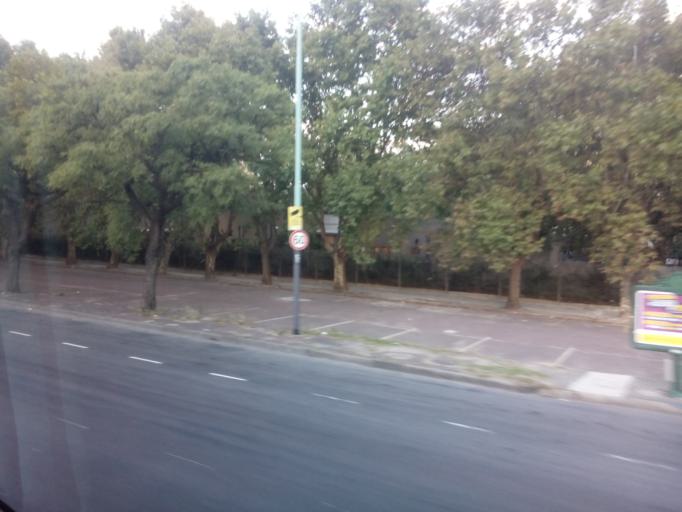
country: AR
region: Buenos Aires F.D.
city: Retiro
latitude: -34.5854
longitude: -58.3724
